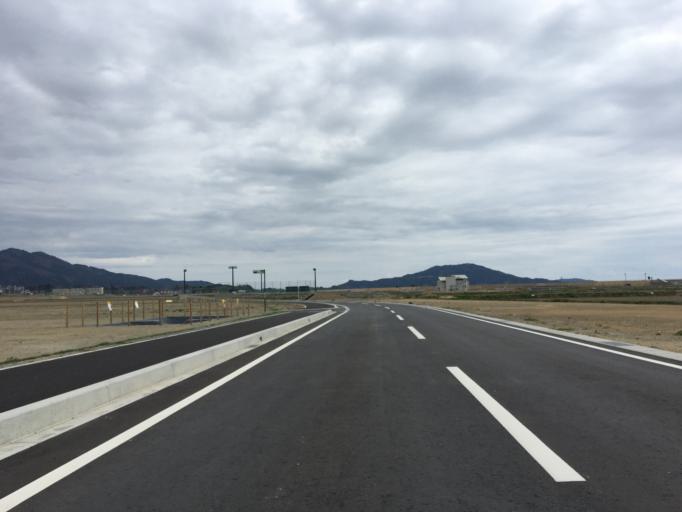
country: JP
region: Iwate
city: Ofunato
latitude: 39.0129
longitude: 141.6256
